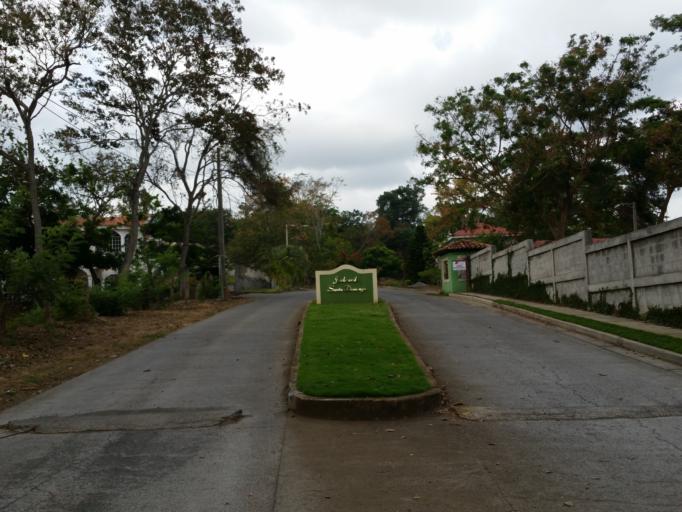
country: NI
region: Masaya
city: Ticuantepe
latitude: 12.0607
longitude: -86.2490
